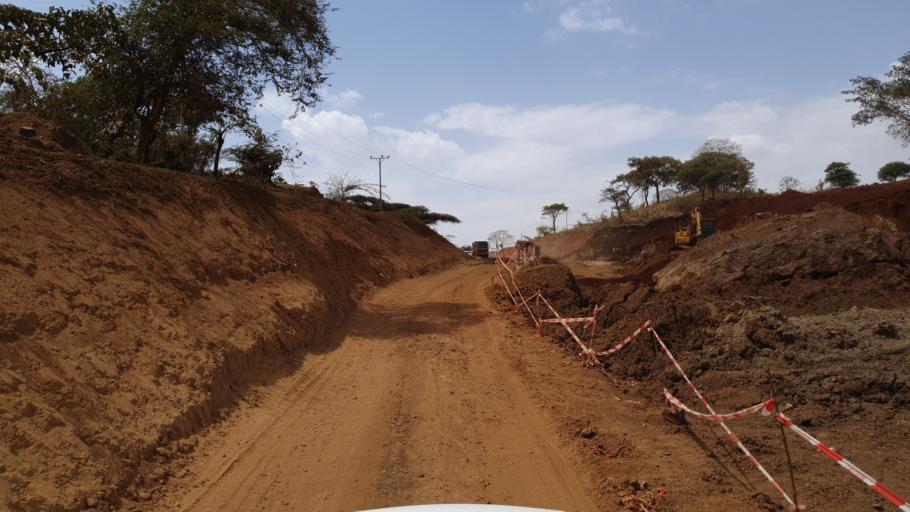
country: ET
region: Oromiya
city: Shambu
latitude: 10.1177
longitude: 36.9208
